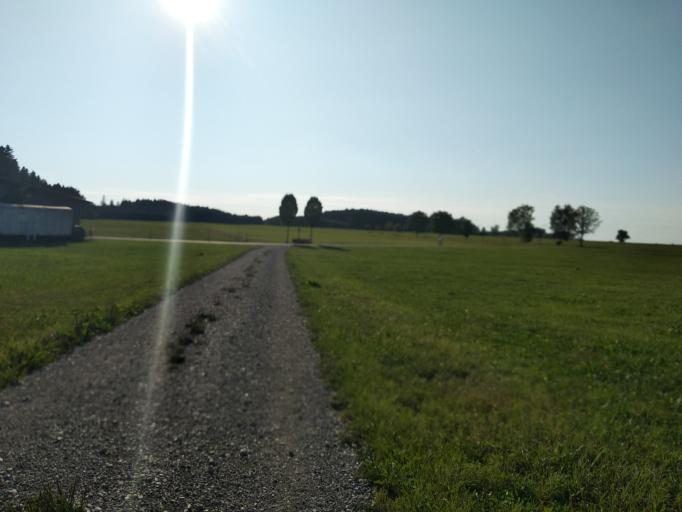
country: DE
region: Bavaria
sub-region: Swabia
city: Legau
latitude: 47.8547
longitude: 10.1213
